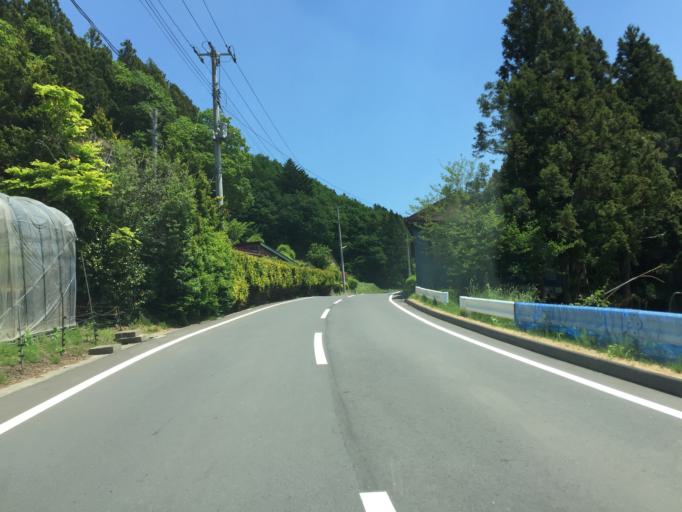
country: JP
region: Fukushima
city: Funehikimachi-funehiki
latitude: 37.5127
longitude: 140.6780
